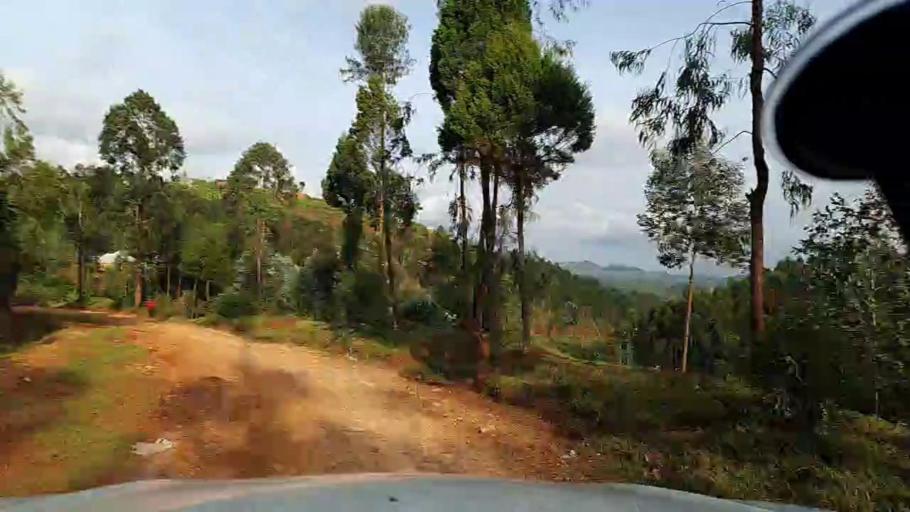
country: RW
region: Southern Province
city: Gitarama
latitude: -2.1861
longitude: 29.5691
